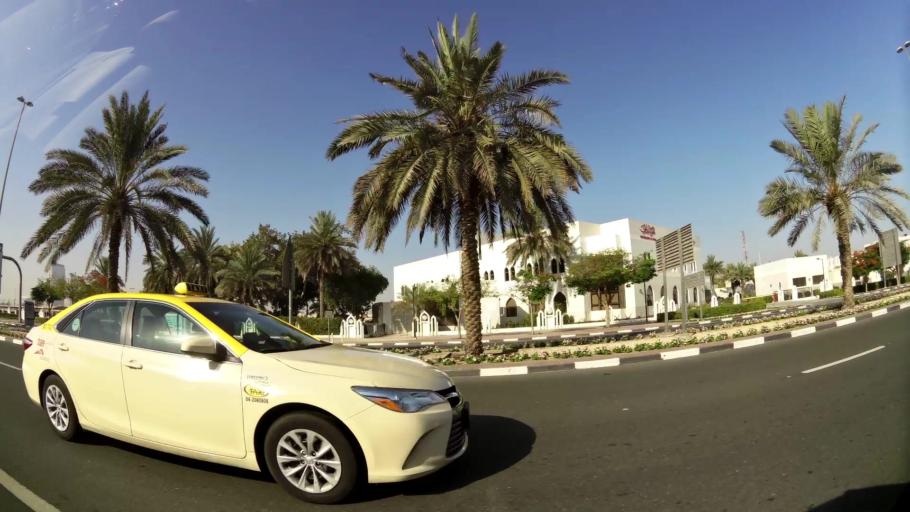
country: AE
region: Ash Shariqah
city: Sharjah
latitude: 25.2476
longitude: 55.3203
